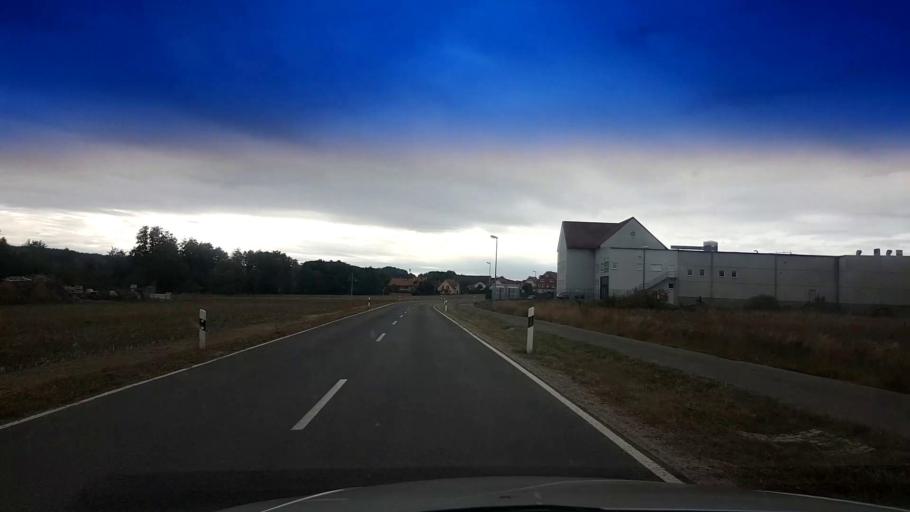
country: DE
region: Bavaria
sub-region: Upper Franconia
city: Stegaurach
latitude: 49.8570
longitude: 10.8648
